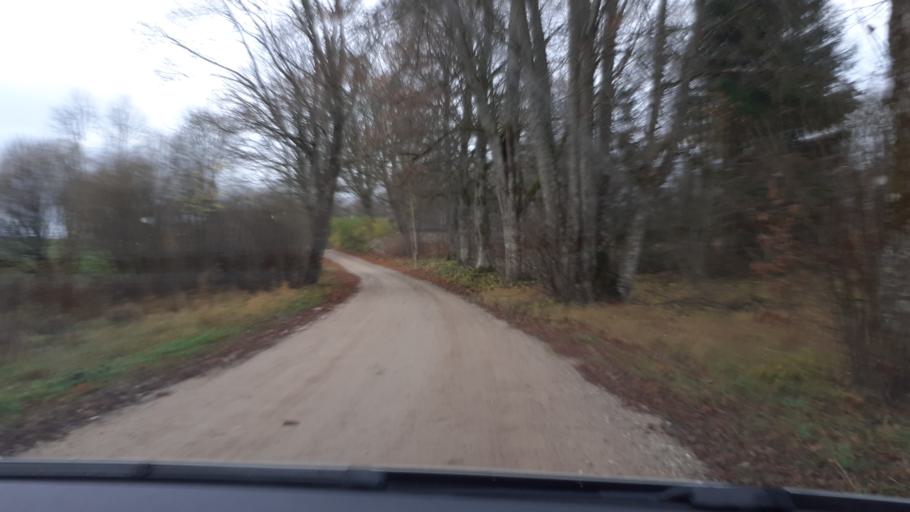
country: LV
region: Aizpute
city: Aizpute
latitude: 56.7731
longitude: 21.8126
